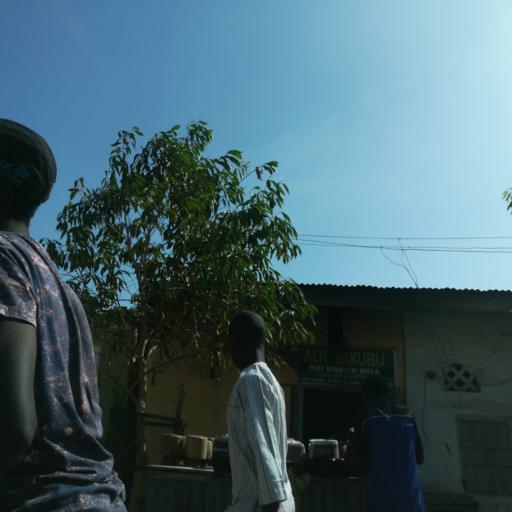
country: NG
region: Kano
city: Kano
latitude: 12.0054
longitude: 8.5192
